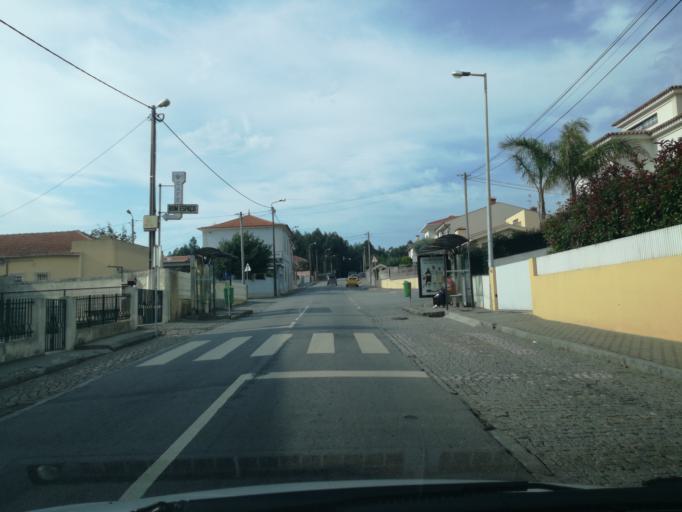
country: PT
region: Porto
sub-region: Vila Nova de Gaia
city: Sao Felix da Marinha
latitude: 41.0251
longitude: -8.6298
